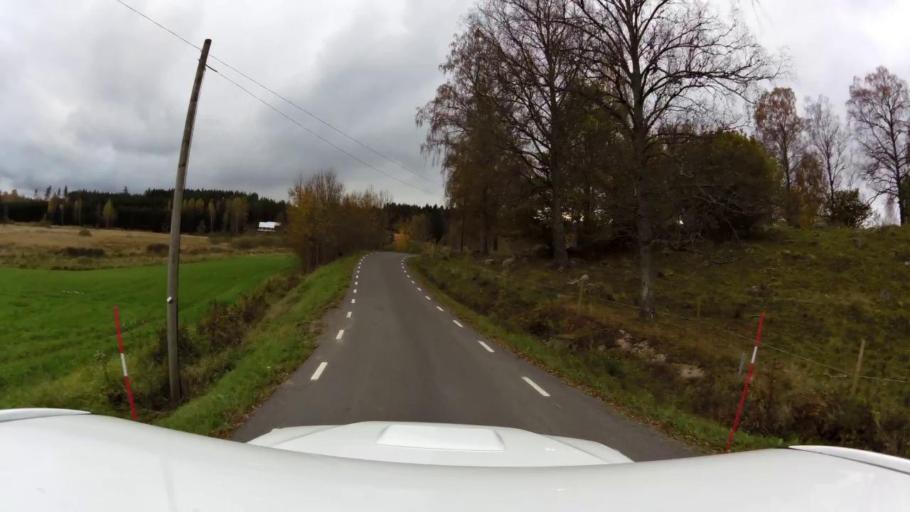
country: SE
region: OEstergoetland
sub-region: Linkopings Kommun
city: Ljungsbro
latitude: 58.5710
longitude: 15.4608
